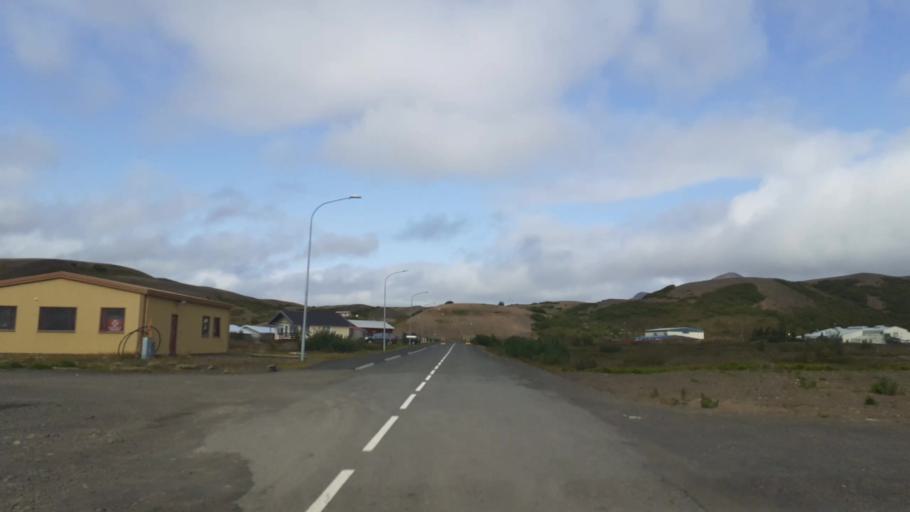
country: IS
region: Northeast
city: Laugar
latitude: 65.6398
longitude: -16.8958
